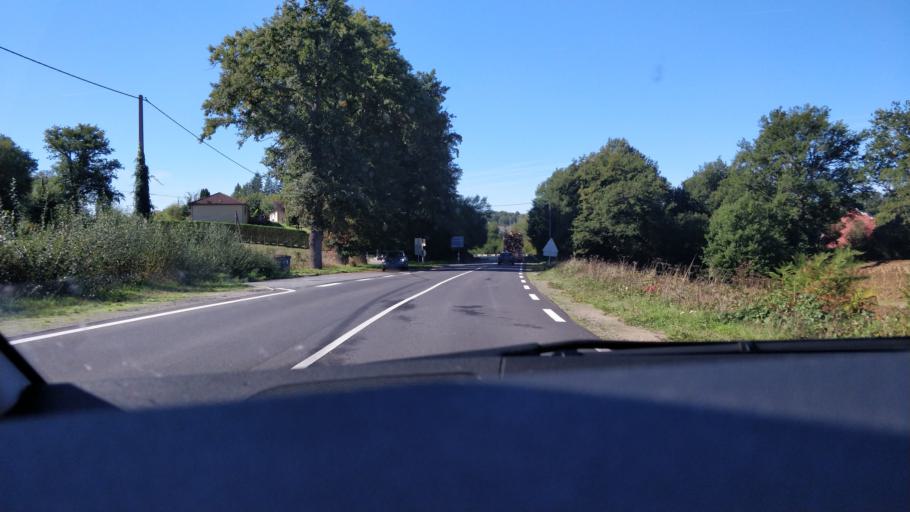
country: FR
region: Limousin
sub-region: Departement de la Haute-Vienne
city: Saint-Leonard-de-Noblat
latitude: 45.8511
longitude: 1.4982
